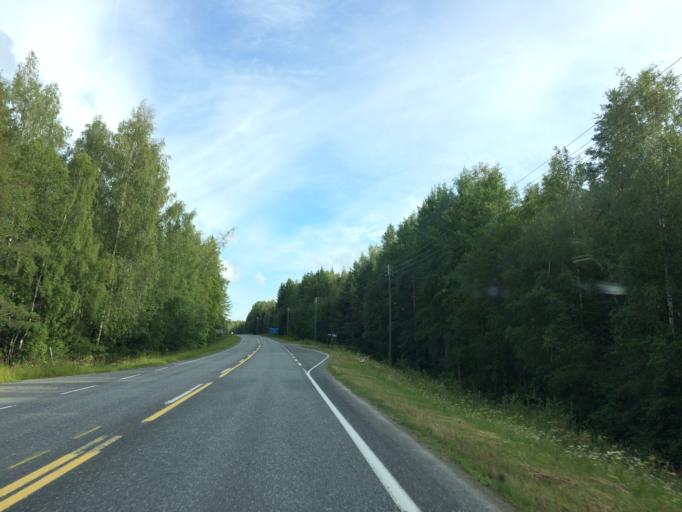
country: FI
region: Haeme
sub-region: Haemeenlinna
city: Janakkala
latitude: 60.9093
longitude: 24.5530
